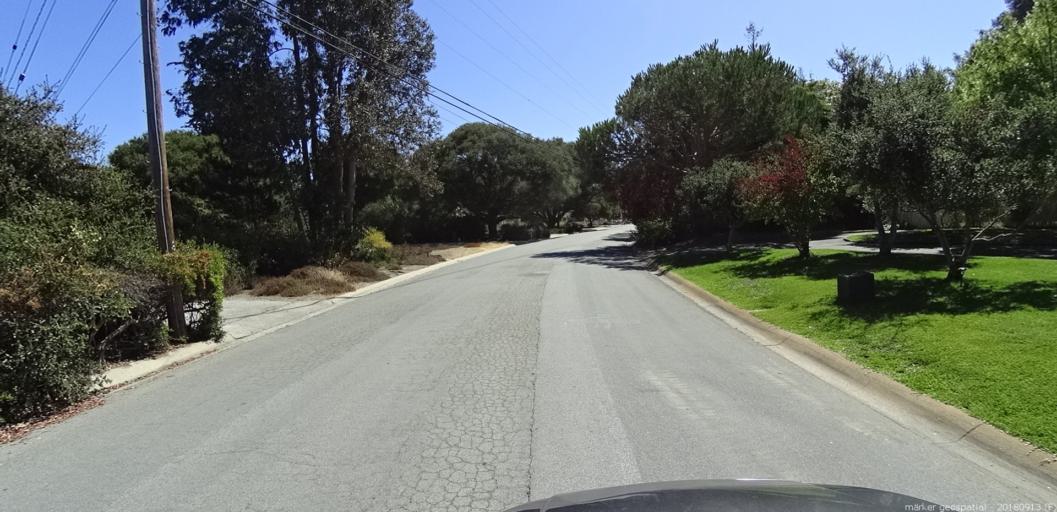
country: US
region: California
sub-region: Monterey County
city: Carmel-by-the-Sea
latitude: 36.5375
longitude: -121.8656
